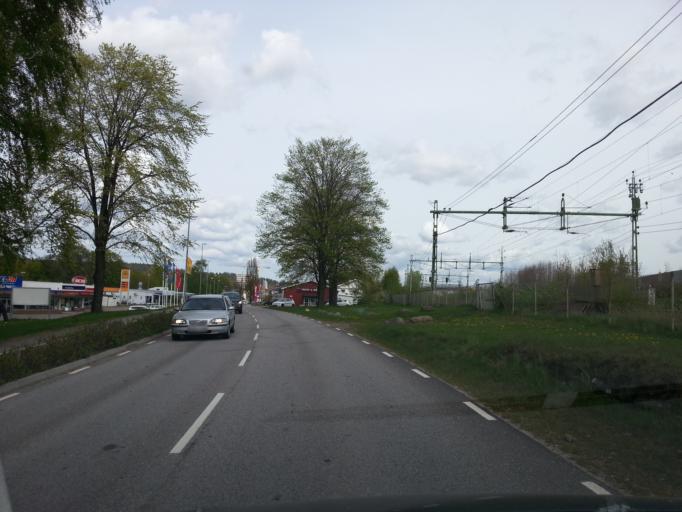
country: SE
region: Vaestra Goetaland
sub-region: Lerums Kommun
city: Lerum
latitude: 57.7653
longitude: 12.2627
